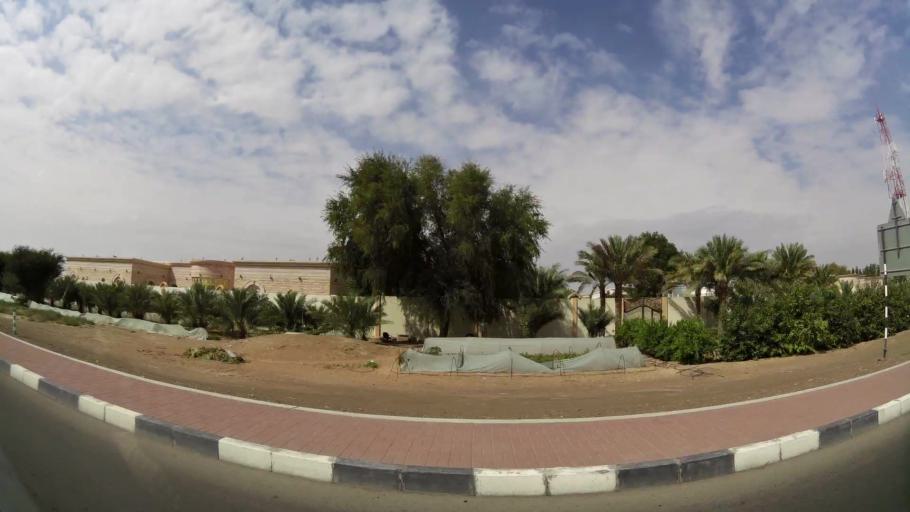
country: AE
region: Abu Dhabi
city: Al Ain
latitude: 24.1937
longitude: 55.7900
